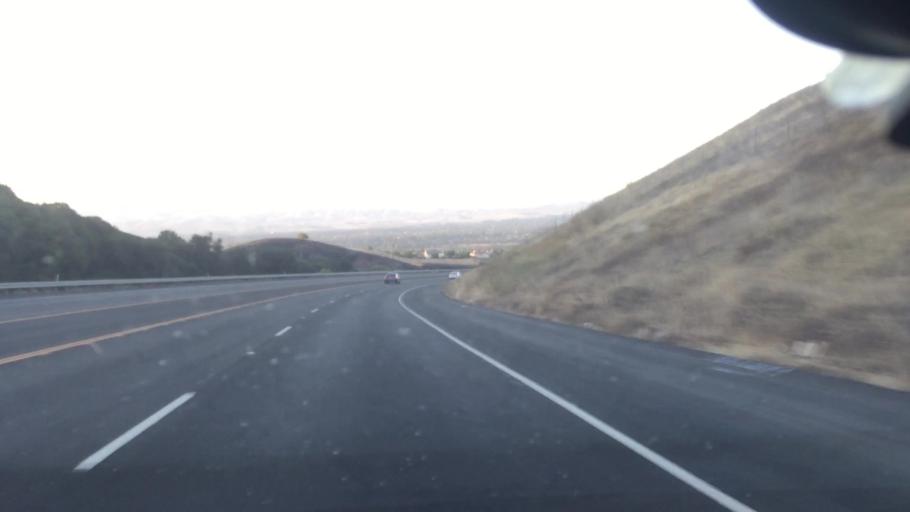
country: US
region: California
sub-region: Alameda County
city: Livermore
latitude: 37.6216
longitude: -121.8077
